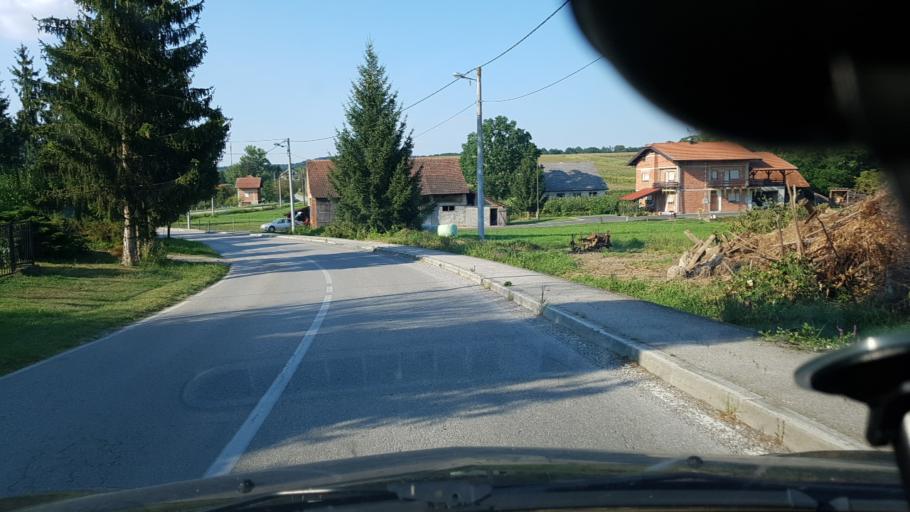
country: HR
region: Zagrebacka
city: Pojatno
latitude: 45.9620
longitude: 15.7364
